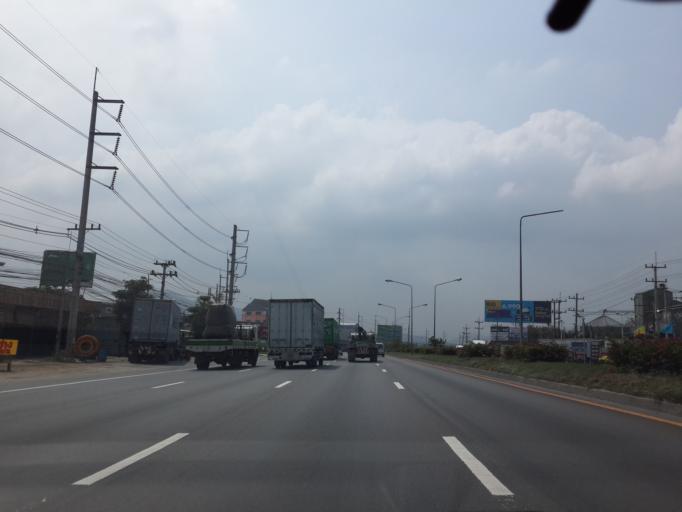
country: TH
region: Chon Buri
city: Chon Buri
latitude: 13.3669
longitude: 101.0184
